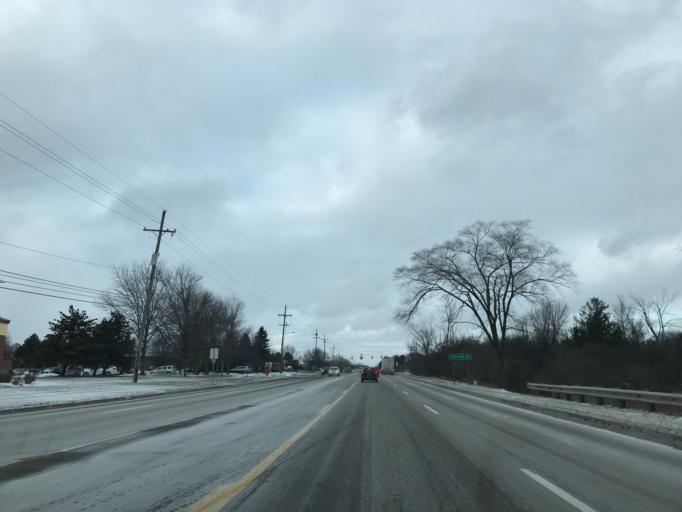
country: US
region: Michigan
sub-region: Wayne County
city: Plymouth
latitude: 42.3936
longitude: -83.4814
